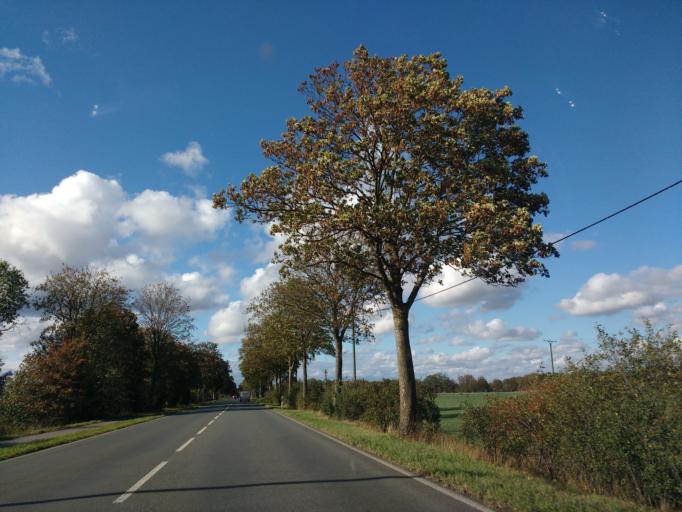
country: DE
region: North Rhine-Westphalia
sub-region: Regierungsbezirk Dusseldorf
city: Alpen
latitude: 51.6168
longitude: 6.5050
